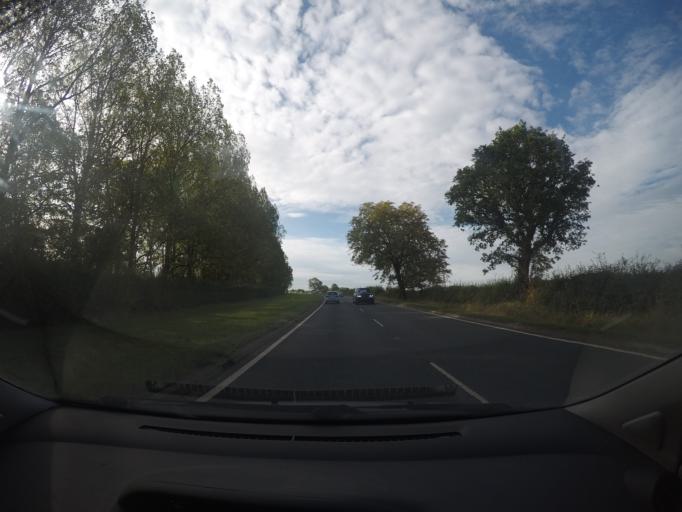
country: GB
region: England
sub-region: North Yorkshire
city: Riccall
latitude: 53.8657
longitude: -1.0508
